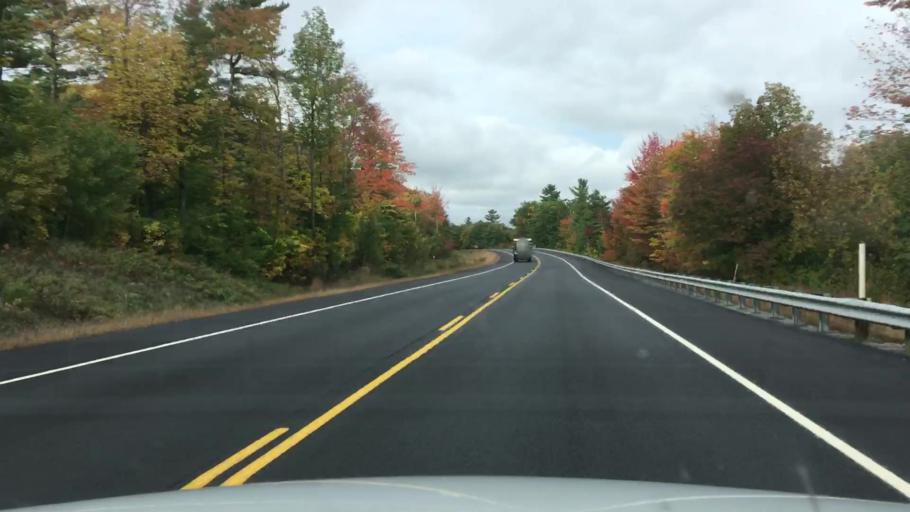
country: US
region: Maine
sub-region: Oxford County
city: Bethel
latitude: 44.3979
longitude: -70.9443
